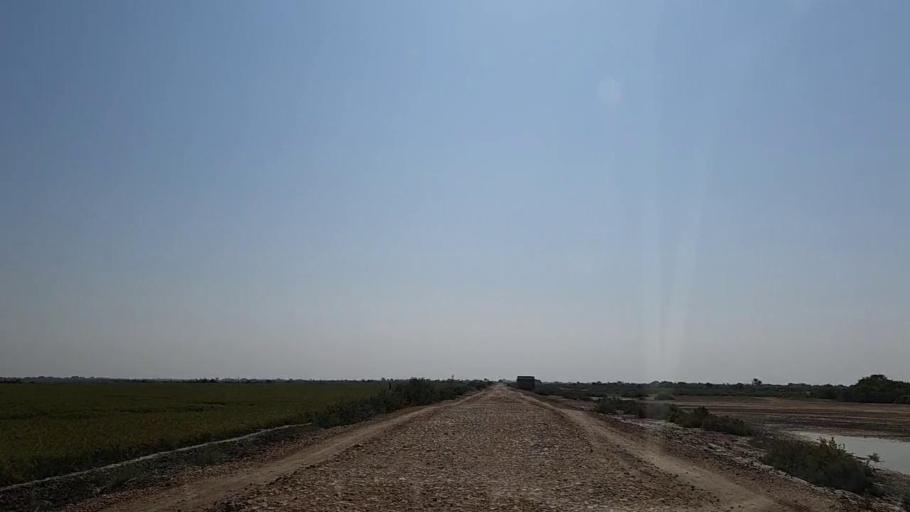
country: PK
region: Sindh
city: Chuhar Jamali
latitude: 24.4730
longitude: 68.0914
